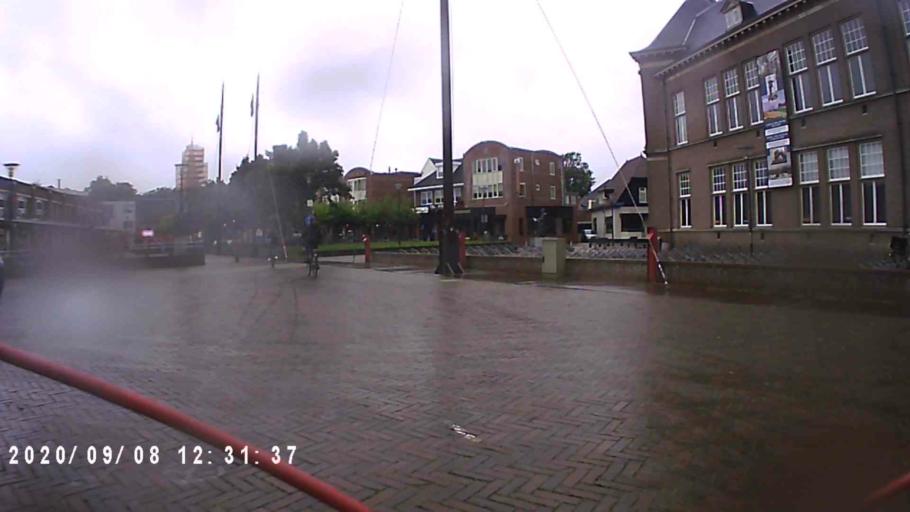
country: NL
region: Groningen
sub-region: Gemeente Veendam
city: Veendam
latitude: 53.1069
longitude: 6.8762
